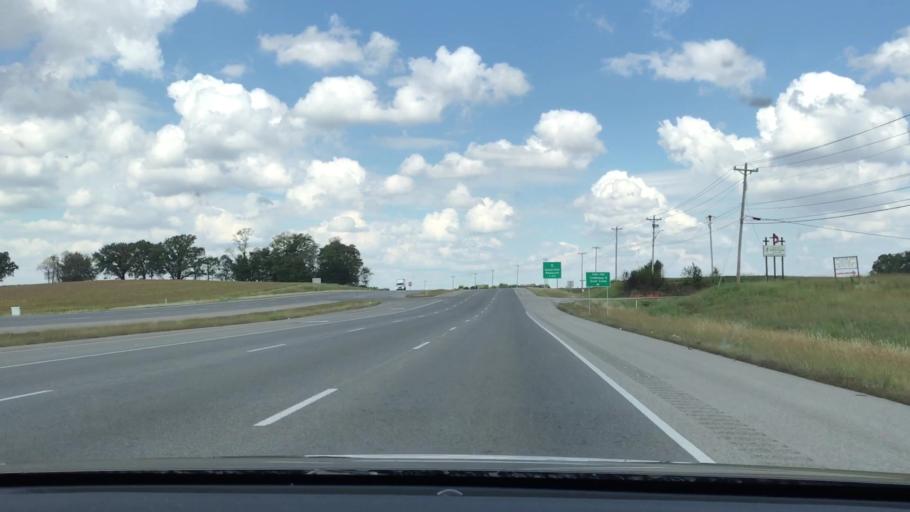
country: US
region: Kentucky
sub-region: Christian County
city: Oak Grove
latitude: 36.6807
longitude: -87.4477
